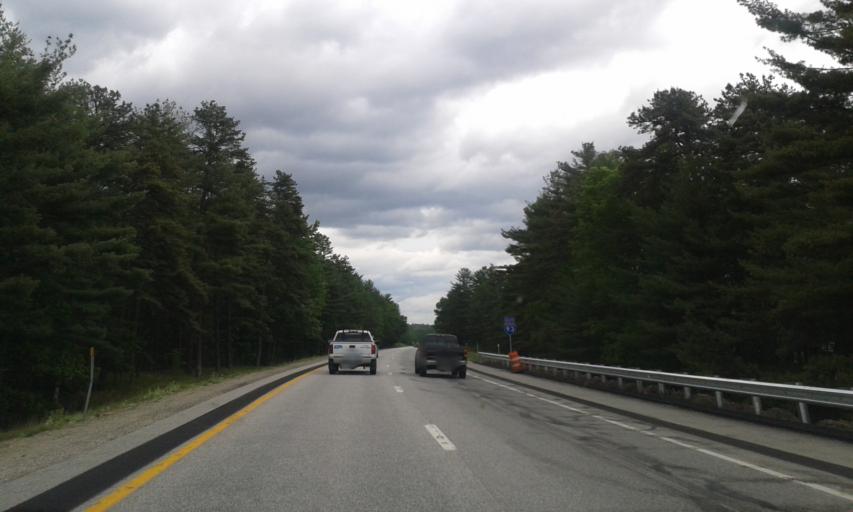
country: US
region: New Hampshire
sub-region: Merrimack County
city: Boscawen
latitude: 43.3286
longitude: -71.6021
